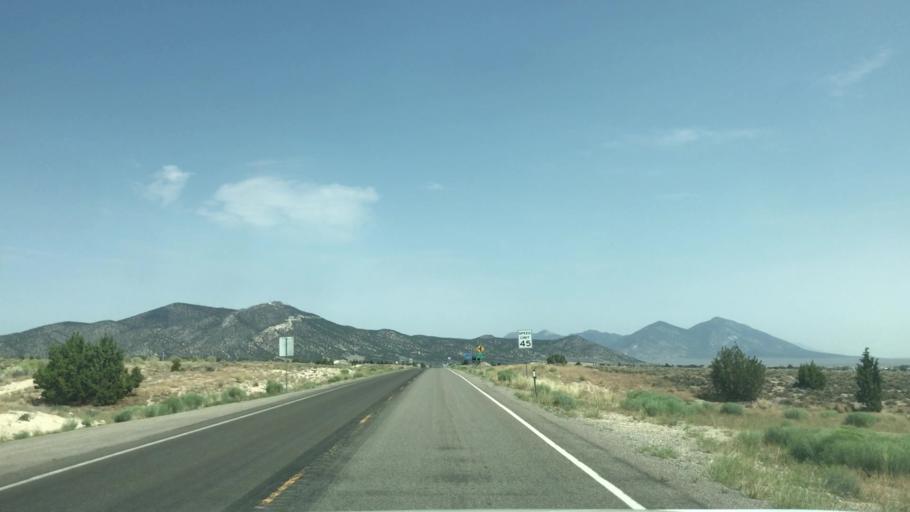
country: US
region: Nevada
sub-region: White Pine County
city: Ely
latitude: 39.2213
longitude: -114.8574
